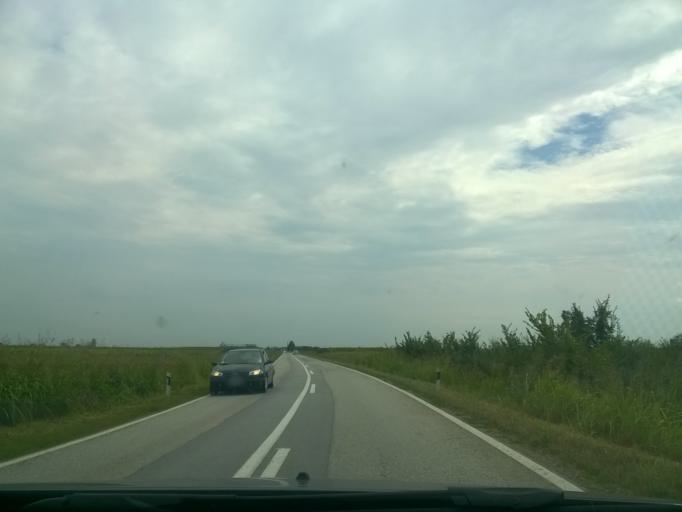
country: RS
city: Neuzina
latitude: 45.3767
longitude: 20.7330
